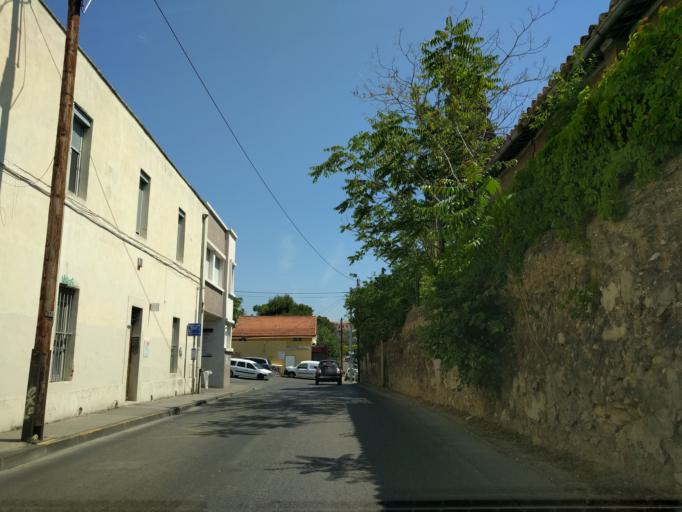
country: FR
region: Provence-Alpes-Cote d'Azur
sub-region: Departement des Bouches-du-Rhone
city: Marseille 13
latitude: 43.3183
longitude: 5.4022
